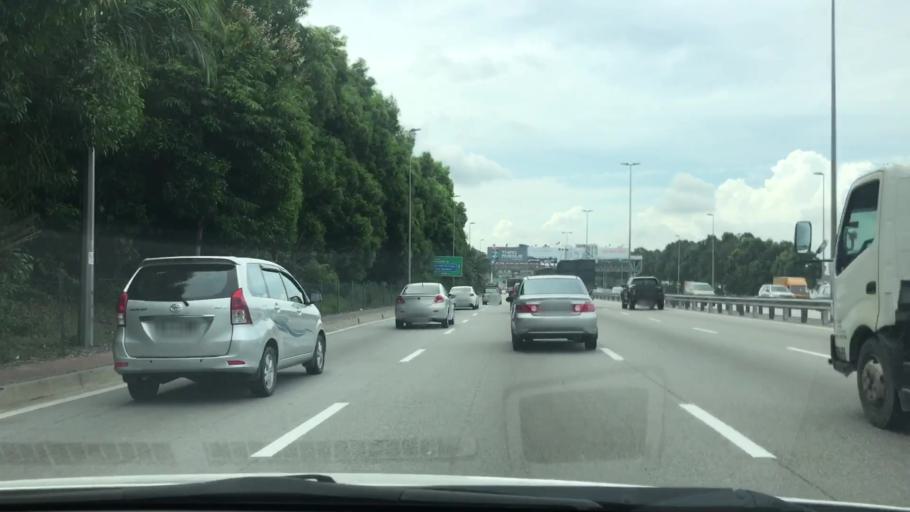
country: MY
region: Selangor
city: Subang Jaya
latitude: 3.0037
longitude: 101.6117
